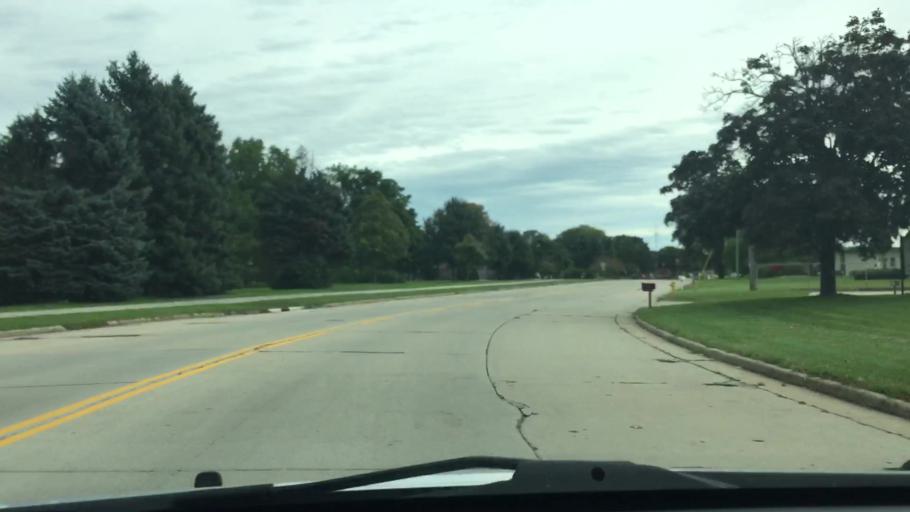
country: US
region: Wisconsin
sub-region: Waukesha County
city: Waukesha
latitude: 43.0028
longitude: -88.2479
